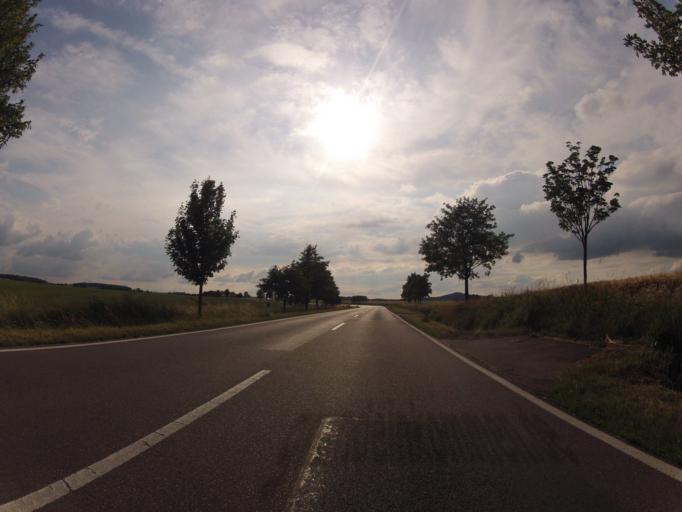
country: DE
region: Saxony
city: Falkenhain
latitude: 51.3928
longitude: 12.8473
